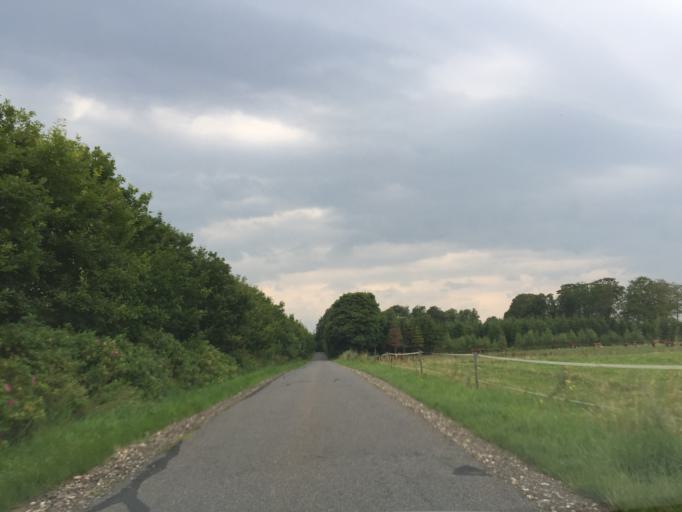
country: DK
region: Central Jutland
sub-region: Viborg Kommune
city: Bjerringbro
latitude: 56.3233
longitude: 9.6658
